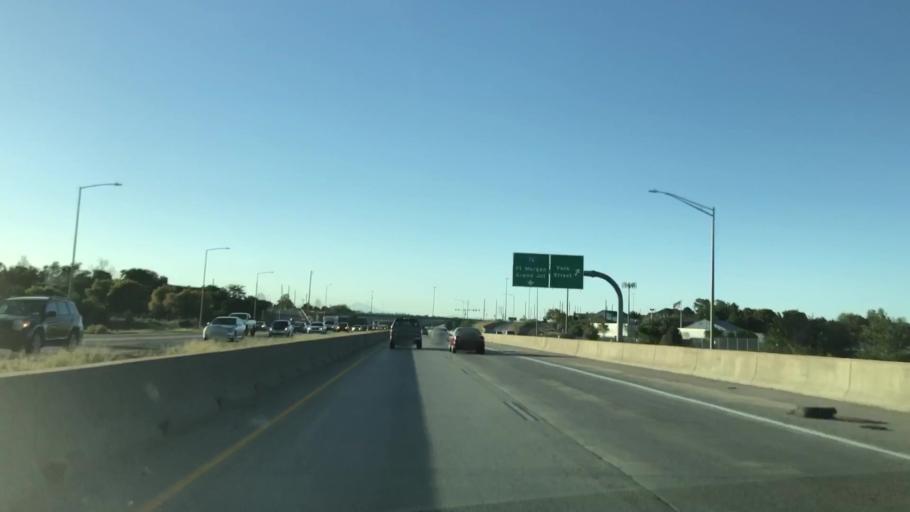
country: US
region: Colorado
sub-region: Adams County
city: Welby
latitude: 39.8170
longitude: -104.9552
